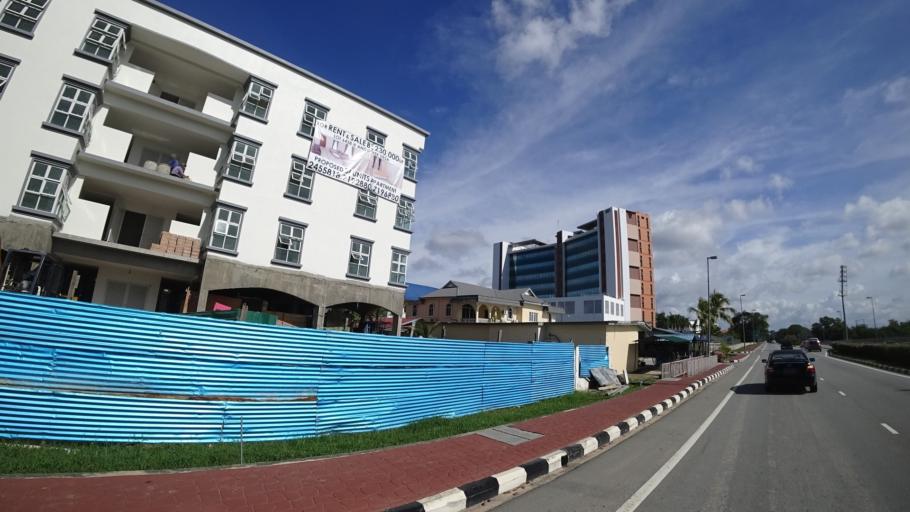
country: BN
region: Brunei and Muara
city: Bandar Seri Begawan
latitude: 4.9388
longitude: 114.9410
